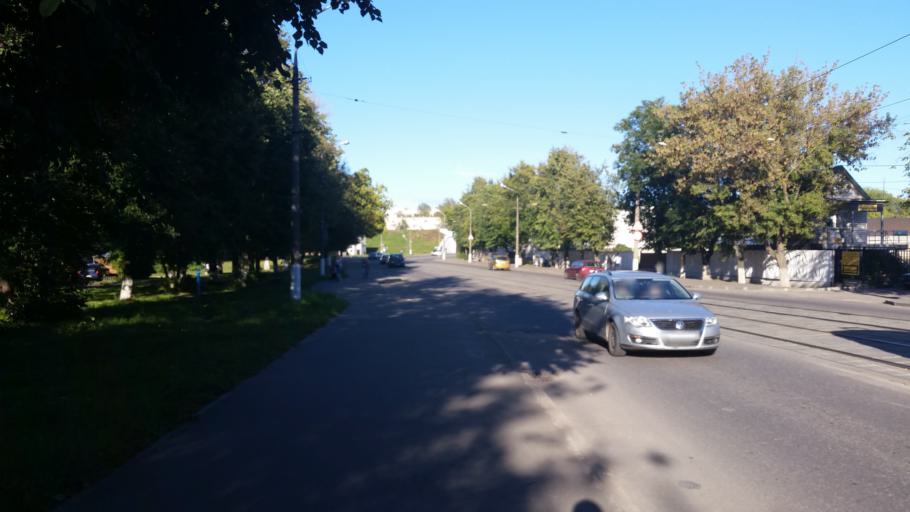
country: BY
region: Vitebsk
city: Vitebsk
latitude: 55.1769
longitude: 30.1830
